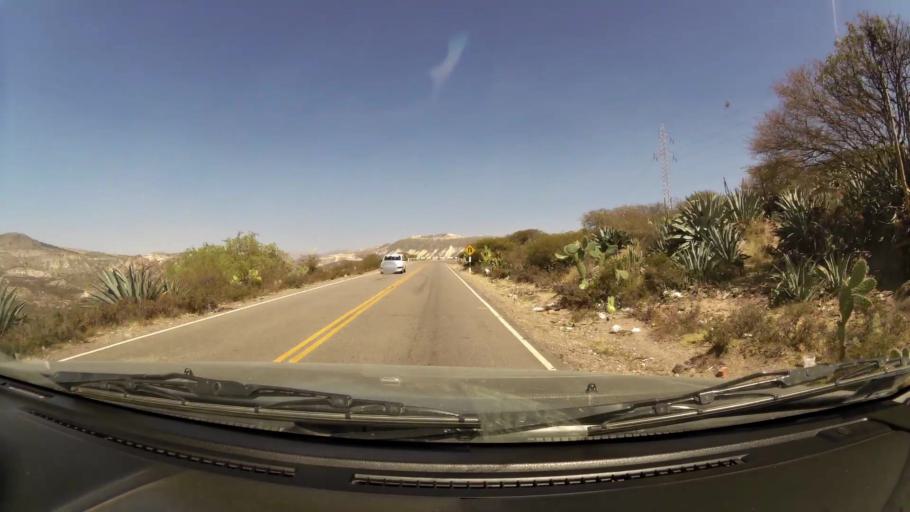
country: PE
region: Ayacucho
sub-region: Provincia de Huamanga
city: Pacaycasa
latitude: -13.0681
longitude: -74.2224
